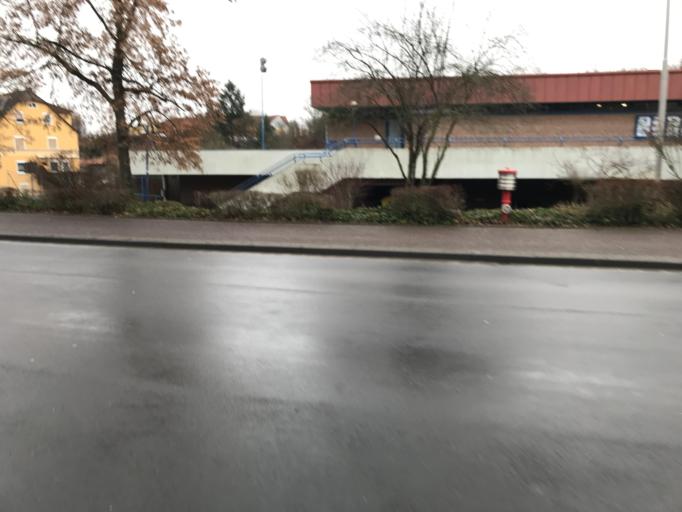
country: DE
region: Hesse
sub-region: Regierungsbezirk Kassel
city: Bad Wildungen
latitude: 51.1156
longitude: 9.1188
